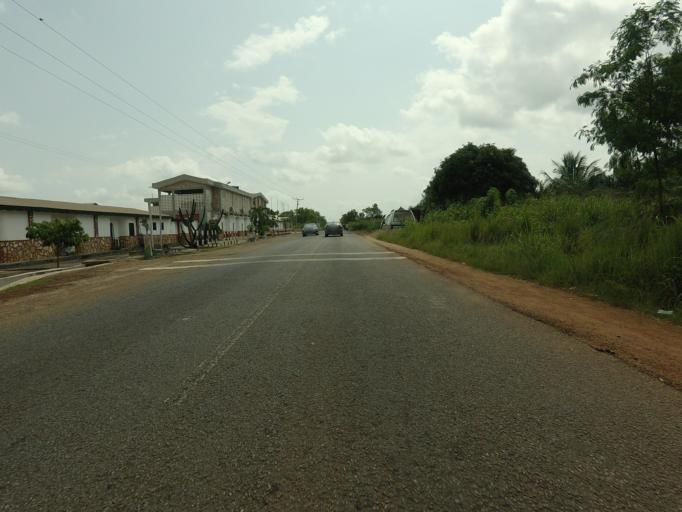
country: TG
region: Maritime
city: Lome
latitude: 6.2266
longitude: 1.0206
